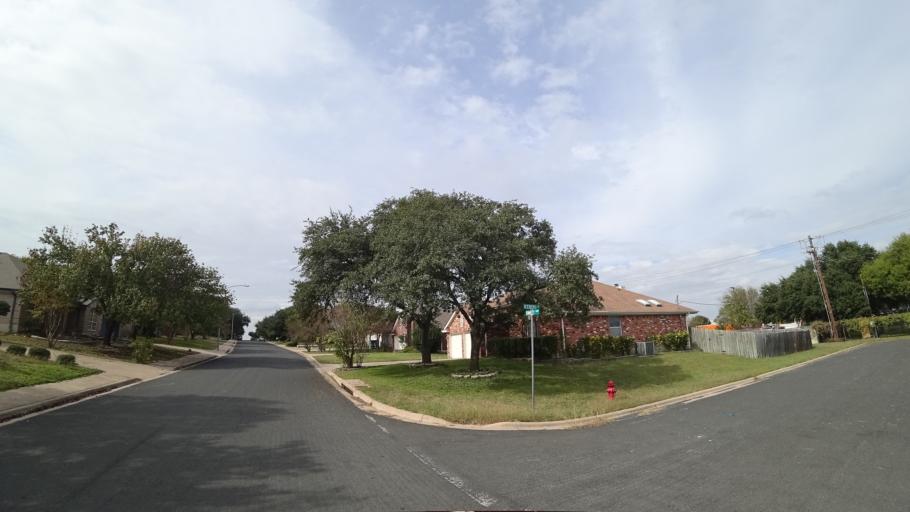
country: US
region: Texas
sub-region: Travis County
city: Wells Branch
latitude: 30.4509
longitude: -97.6747
